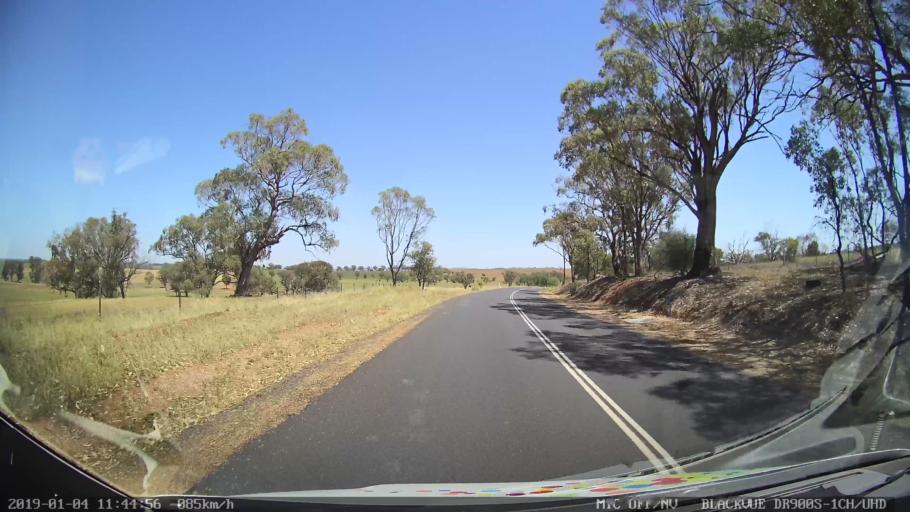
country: AU
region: New South Wales
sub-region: Cabonne
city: Molong
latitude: -32.9596
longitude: 148.7662
